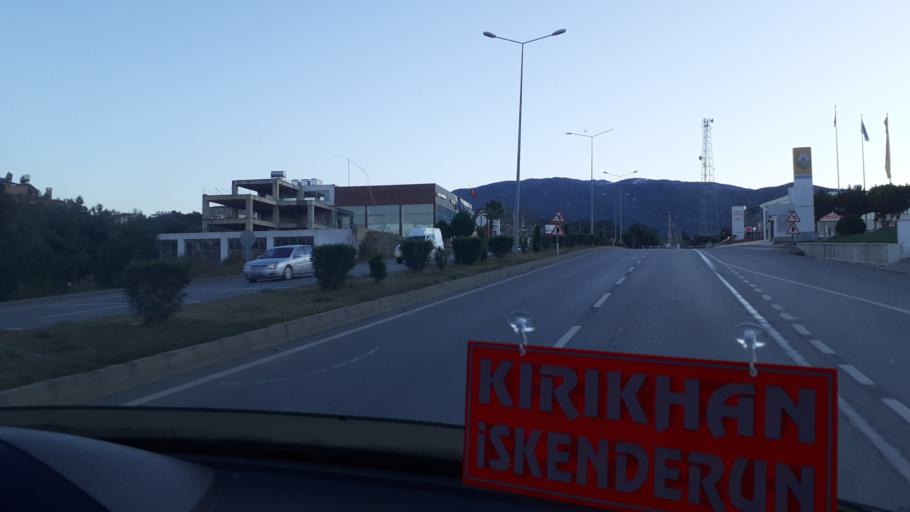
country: TR
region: Hatay
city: Cirtiman
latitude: 36.5362
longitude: 36.1468
